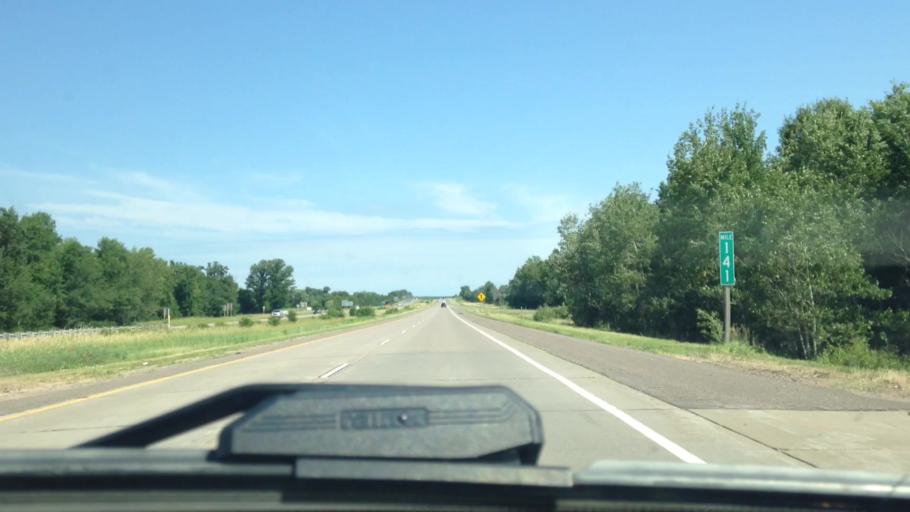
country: US
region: Wisconsin
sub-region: Barron County
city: Rice Lake
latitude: 45.4734
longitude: -91.7587
